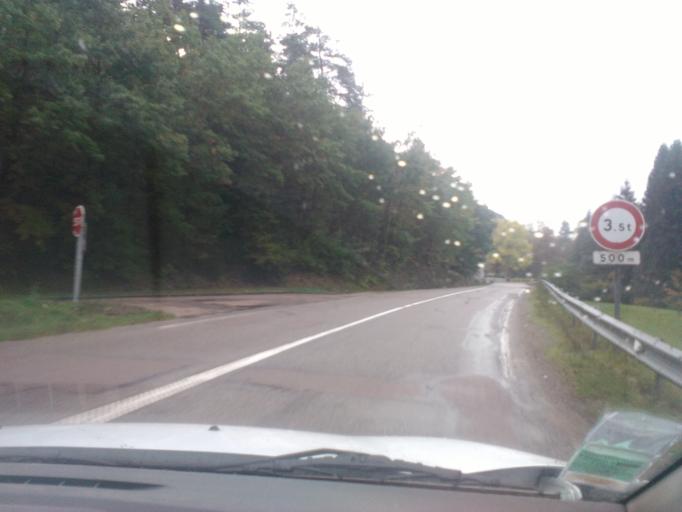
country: FR
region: Lorraine
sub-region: Departement des Vosges
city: Bruyeres
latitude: 48.2209
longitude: 6.7229
